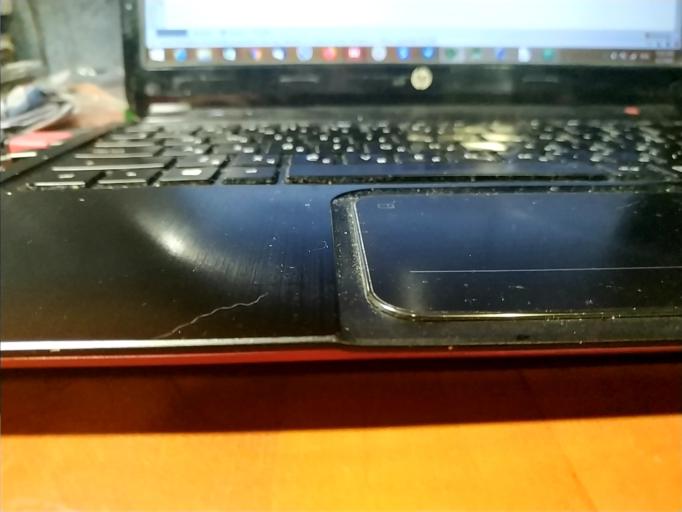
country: RU
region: Vologda
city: Suda
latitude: 58.9140
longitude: 37.5432
